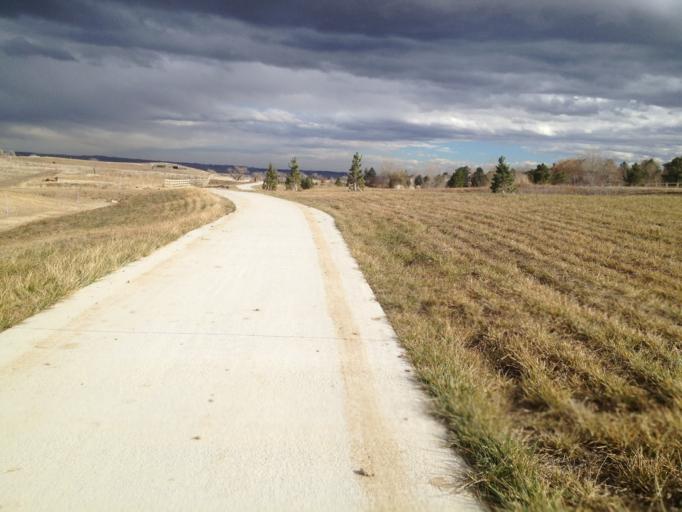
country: US
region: Colorado
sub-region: Boulder County
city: Superior
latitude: 39.9474
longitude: -105.1593
